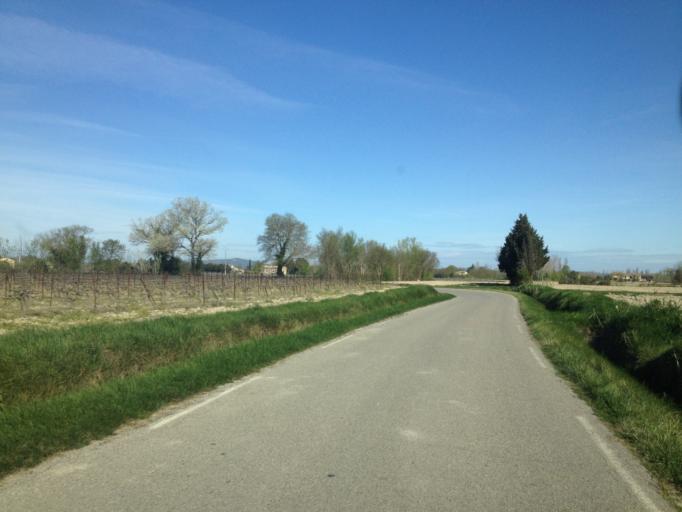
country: FR
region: Provence-Alpes-Cote d'Azur
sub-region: Departement du Vaucluse
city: Caderousse
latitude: 44.0973
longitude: 4.7706
